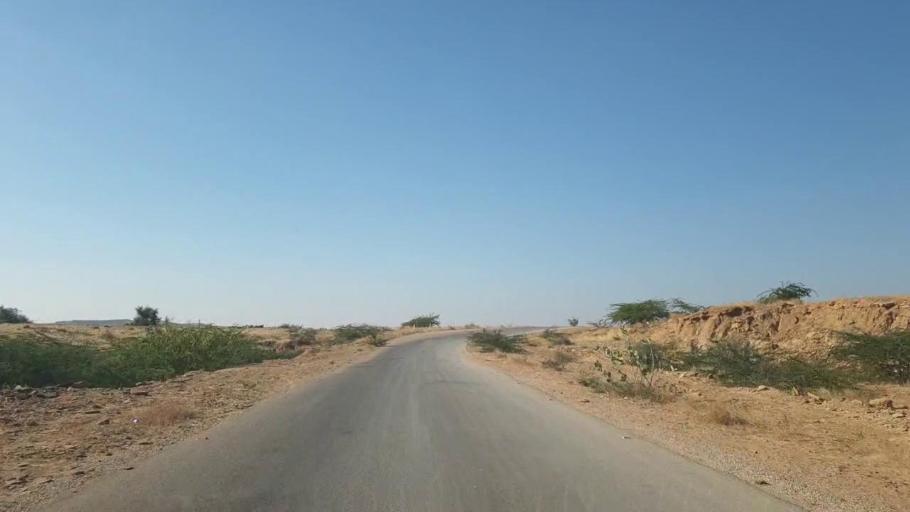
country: PK
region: Sindh
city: Malir Cantonment
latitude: 25.2846
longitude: 67.5781
